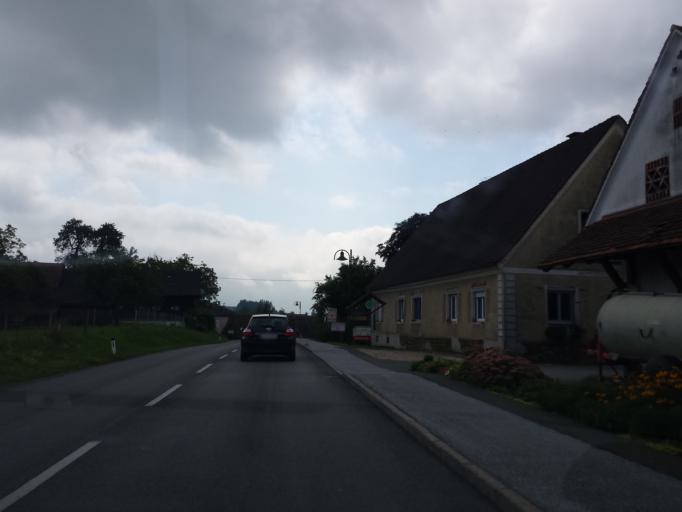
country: AT
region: Styria
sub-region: Politischer Bezirk Deutschlandsberg
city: Rassach
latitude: 46.8607
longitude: 15.2669
